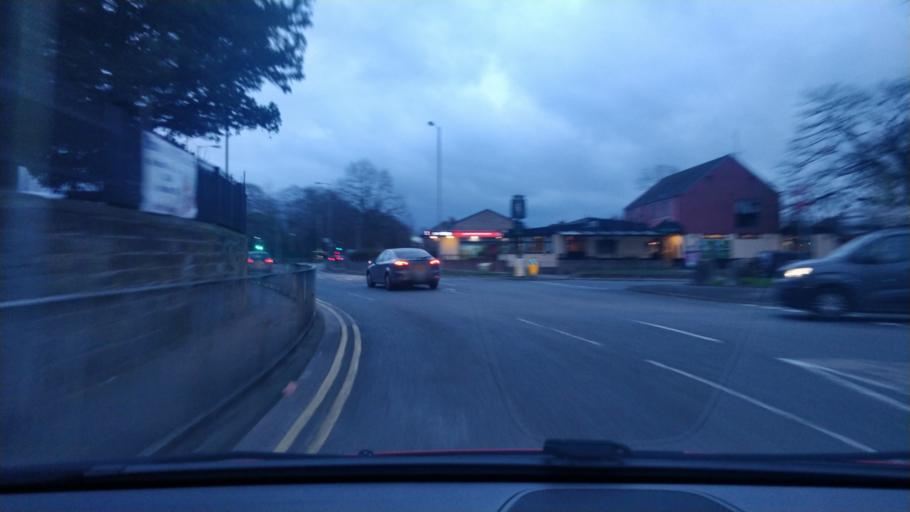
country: GB
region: England
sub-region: Knowsley
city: Knowsley
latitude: 53.4249
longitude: -2.8896
